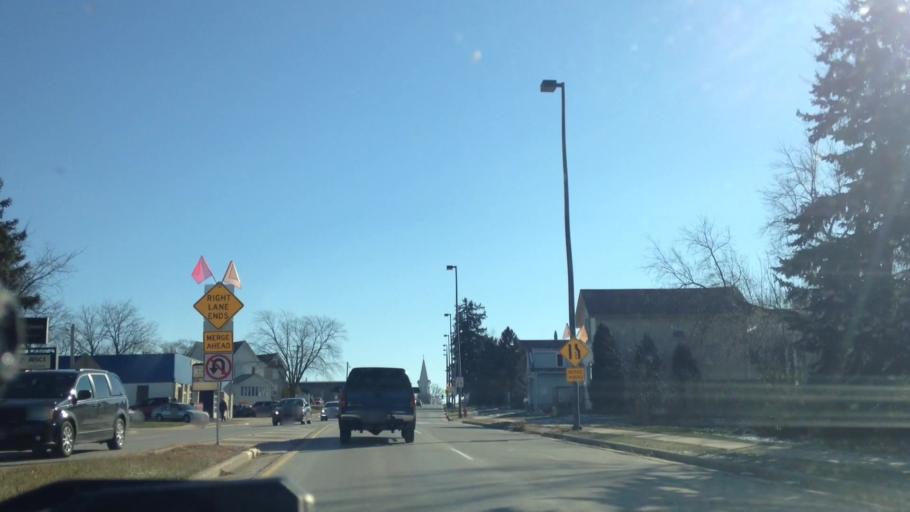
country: US
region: Wisconsin
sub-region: Waukesha County
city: Menomonee Falls
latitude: 43.1832
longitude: -88.1227
